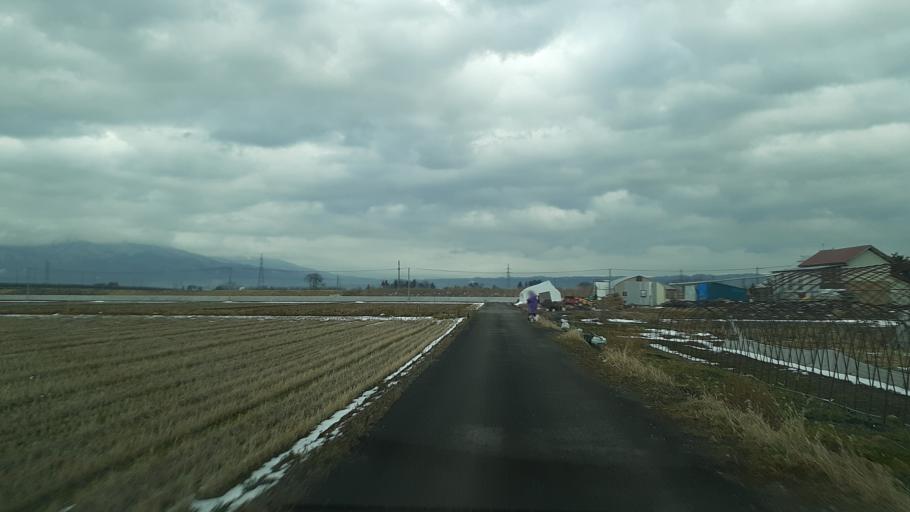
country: JP
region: Fukushima
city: Kitakata
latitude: 37.5539
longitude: 139.8529
